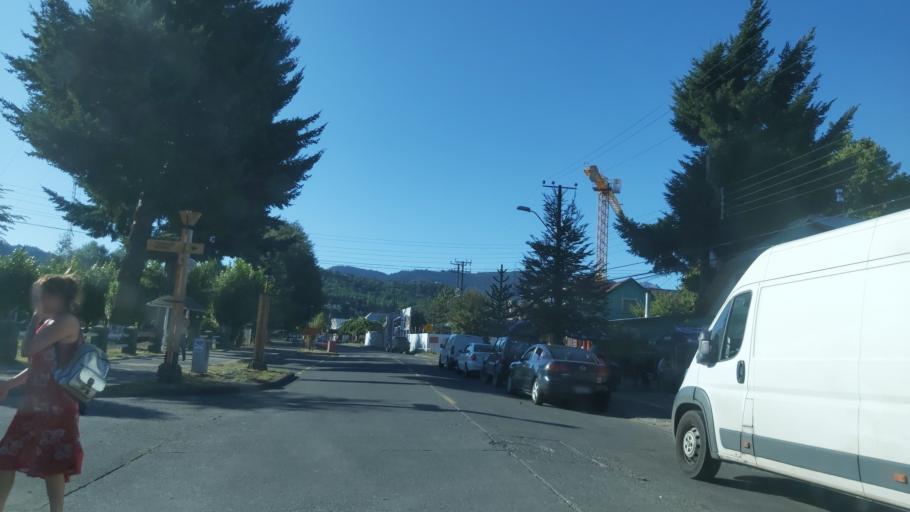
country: AR
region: Neuquen
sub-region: Departamento de Loncopue
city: Loncopue
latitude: -38.4534
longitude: -71.3702
